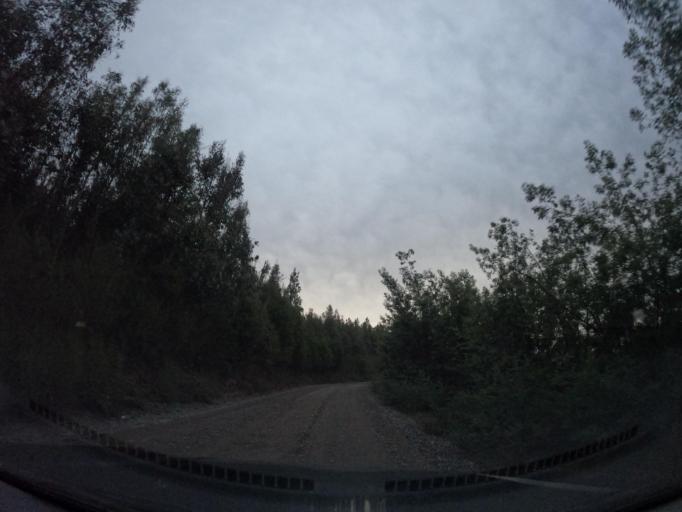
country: CL
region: Biobio
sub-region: Provincia de Concepcion
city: Chiguayante
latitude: -37.0122
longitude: -72.8771
